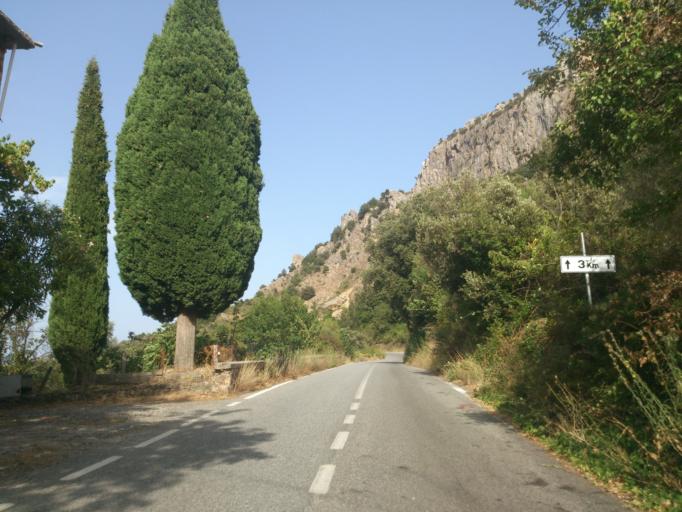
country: IT
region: Calabria
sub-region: Provincia di Reggio Calabria
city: Pazzano
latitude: 38.4700
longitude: 16.4400
